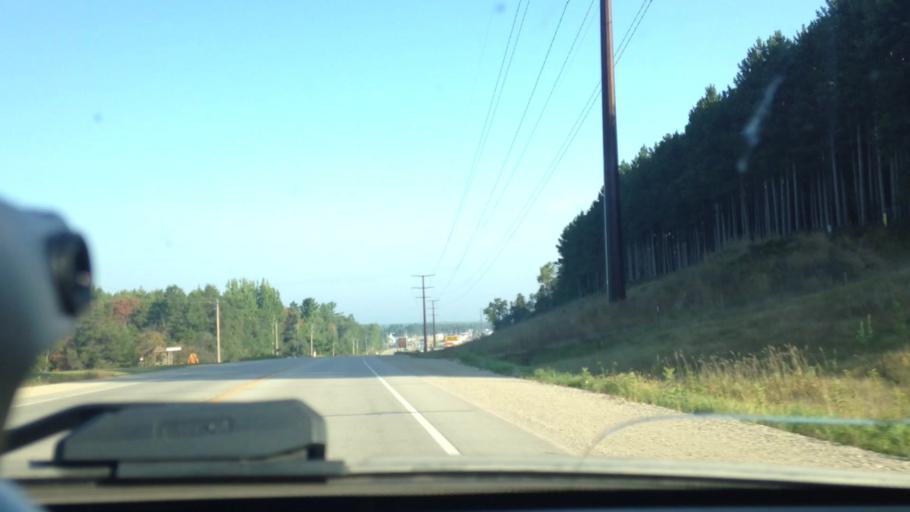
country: US
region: Wisconsin
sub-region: Marinette County
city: Peshtigo
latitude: 45.2139
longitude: -87.9957
